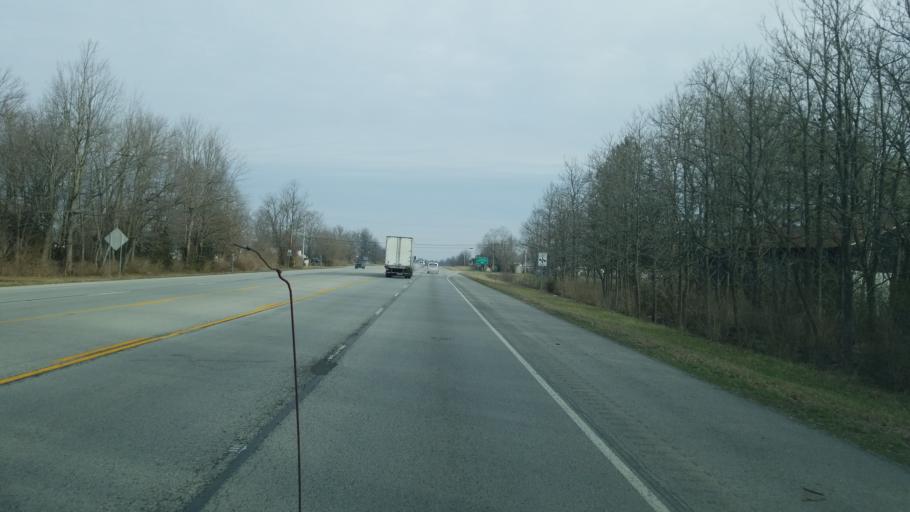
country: US
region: Kentucky
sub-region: Boyle County
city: Junction City
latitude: 37.5838
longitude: -84.7858
